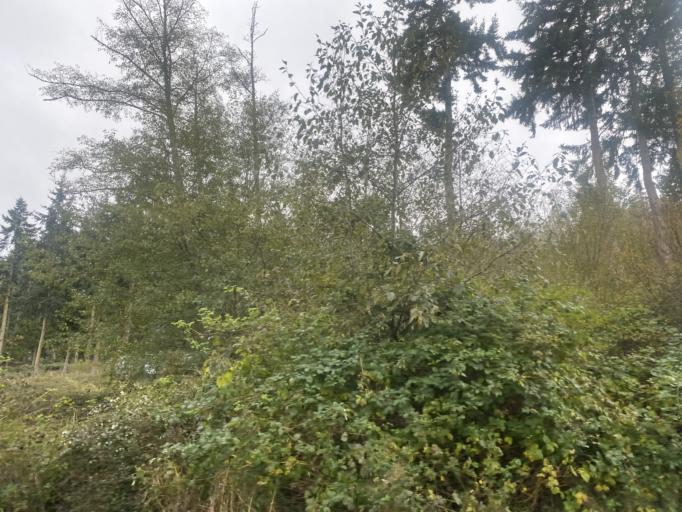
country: US
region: Washington
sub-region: Island County
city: Freeland
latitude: 48.0858
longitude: -122.5620
